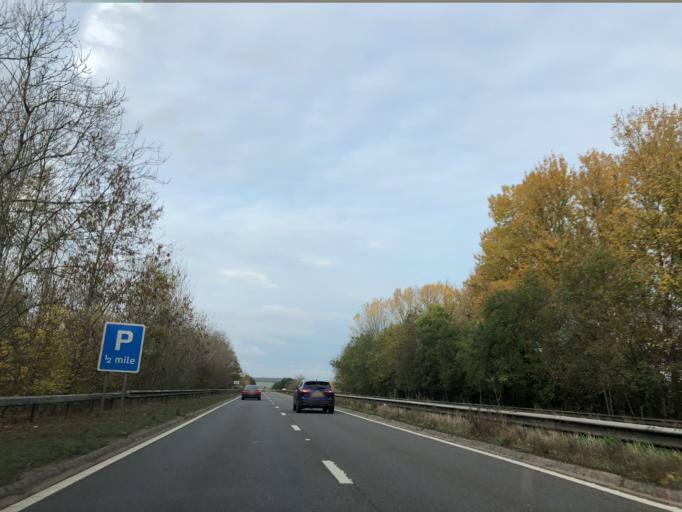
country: GB
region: England
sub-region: Buckinghamshire
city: Marlow
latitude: 51.5643
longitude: -0.7632
